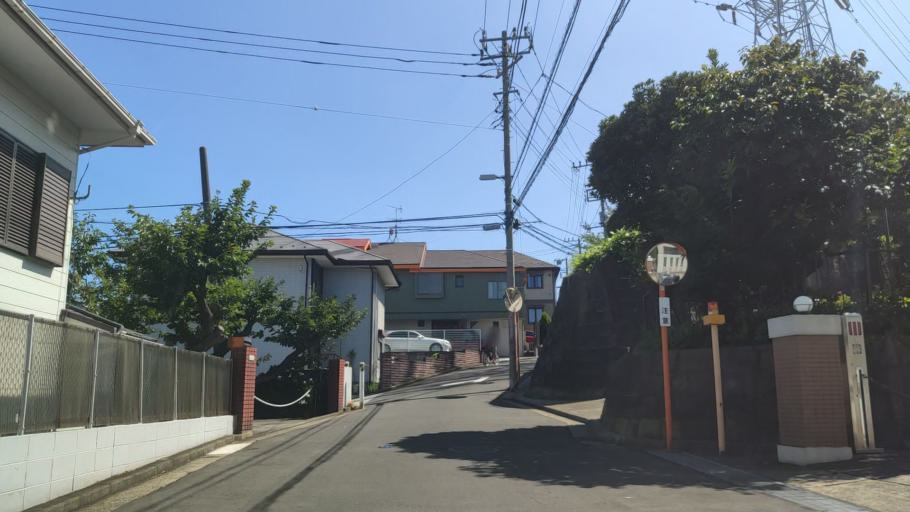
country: JP
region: Kanagawa
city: Yokohama
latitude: 35.5163
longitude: 139.6354
